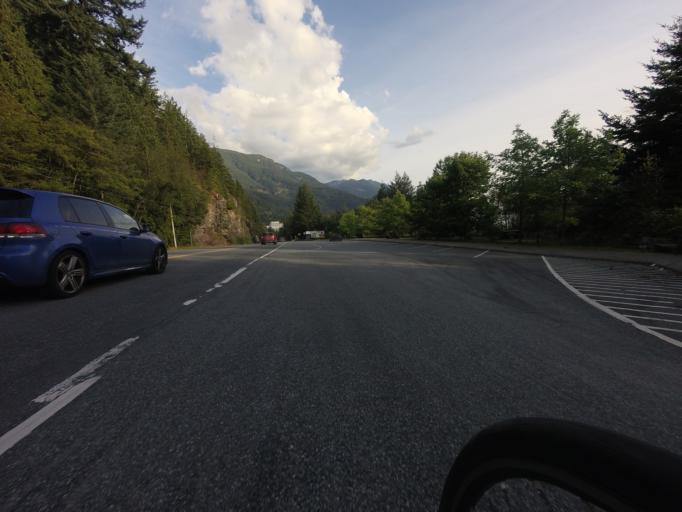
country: CA
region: British Columbia
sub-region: Greater Vancouver Regional District
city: Lions Bay
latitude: 49.6350
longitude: -123.2103
